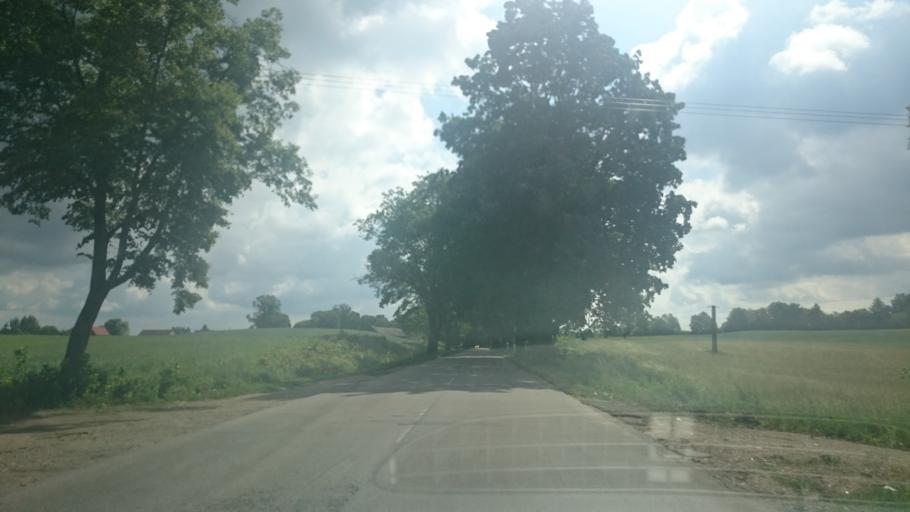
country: PL
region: Pomeranian Voivodeship
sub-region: Powiat starogardzki
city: Kaliska
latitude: 53.9677
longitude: 18.2568
